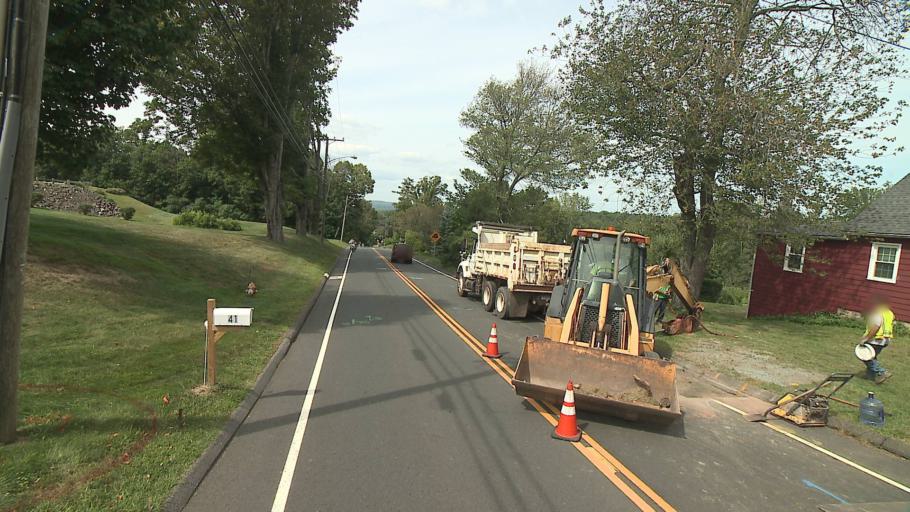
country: US
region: Connecticut
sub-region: Litchfield County
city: Plymouth
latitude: 41.6671
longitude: -73.0509
